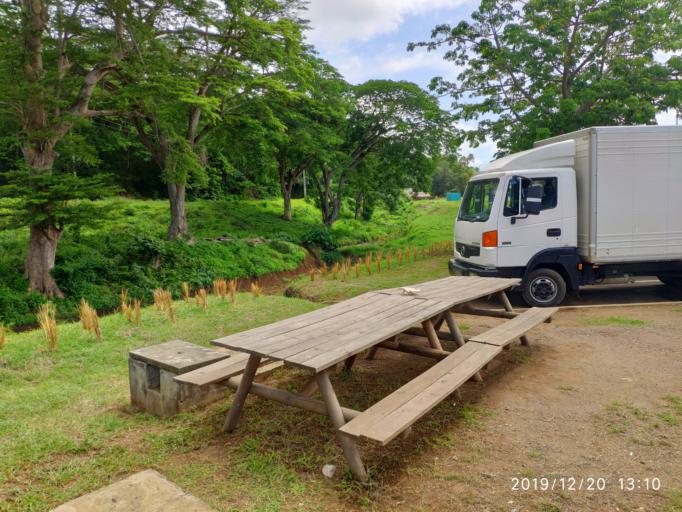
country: MG
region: Diana
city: Hell-Ville
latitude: -13.3192
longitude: 48.3108
